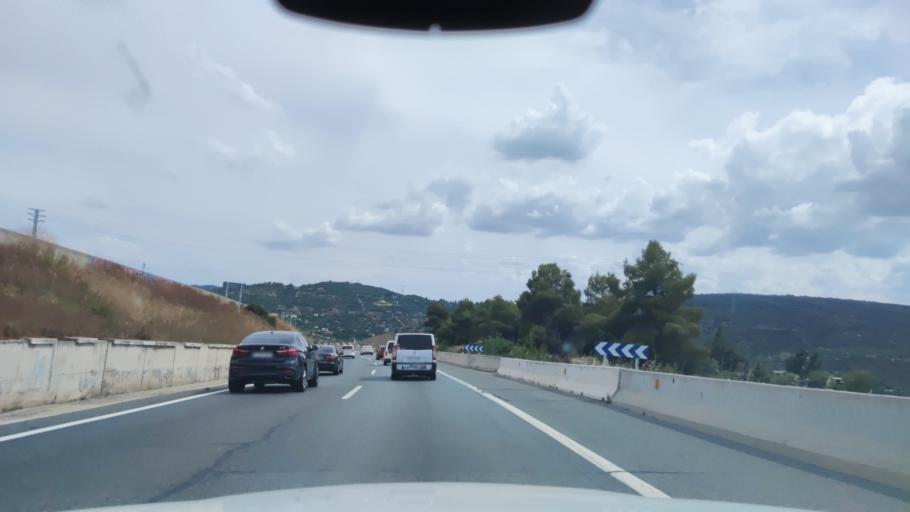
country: ES
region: Madrid
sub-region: Provincia de Madrid
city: Perales de Tajuna
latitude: 40.2353
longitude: -3.3440
